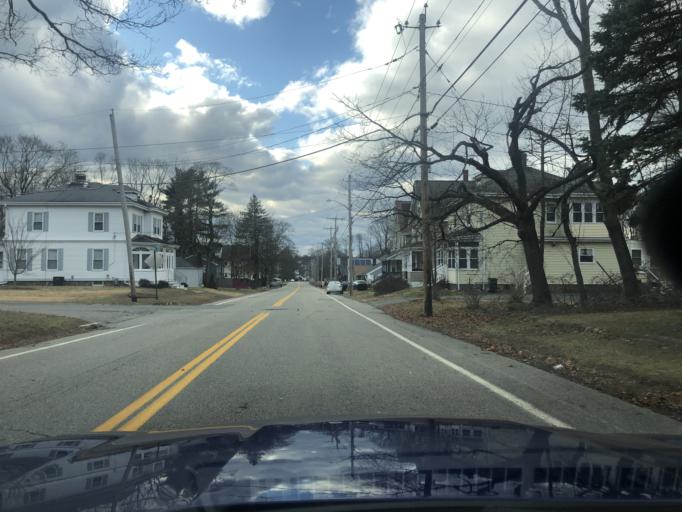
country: US
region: Massachusetts
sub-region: Plymouth County
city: Brockton
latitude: 42.1083
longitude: -71.0094
